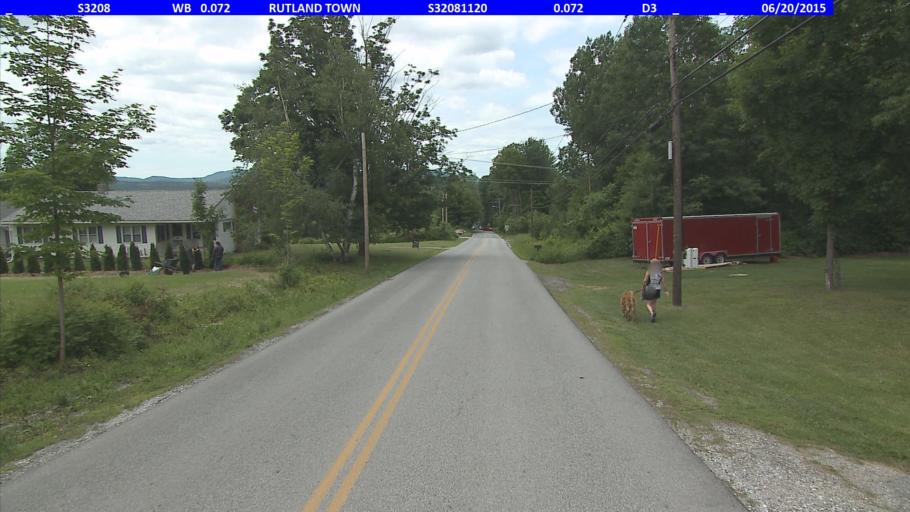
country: US
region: Vermont
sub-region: Rutland County
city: Rutland
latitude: 43.6085
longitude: -72.9440
